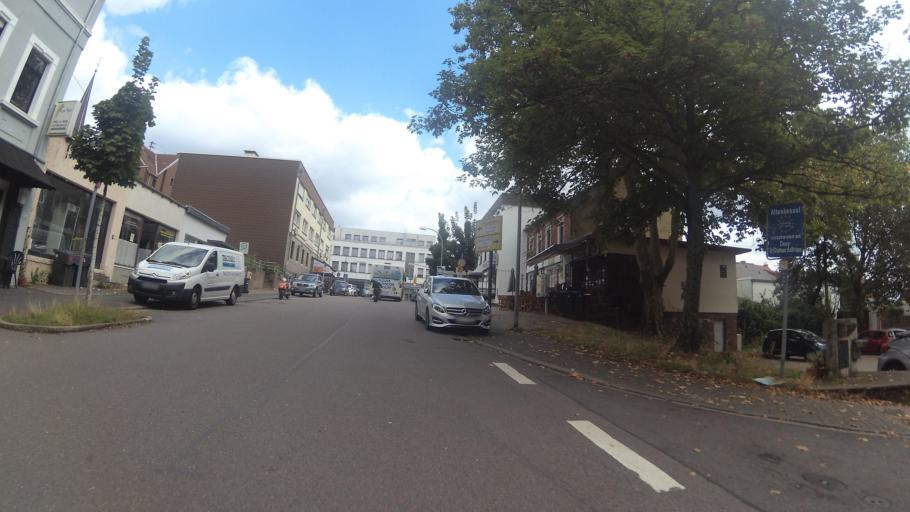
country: DE
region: Saarland
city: Puttlingen
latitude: 49.2620
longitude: 6.9162
